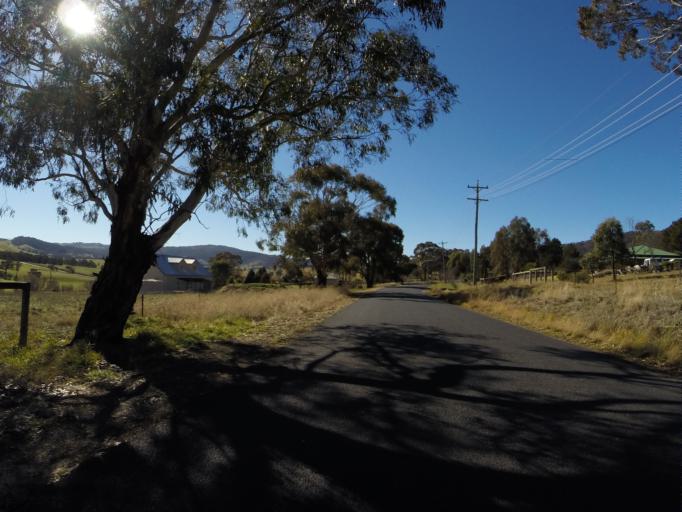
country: AU
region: New South Wales
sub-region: Oberon
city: Oberon
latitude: -33.5259
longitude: 149.9051
